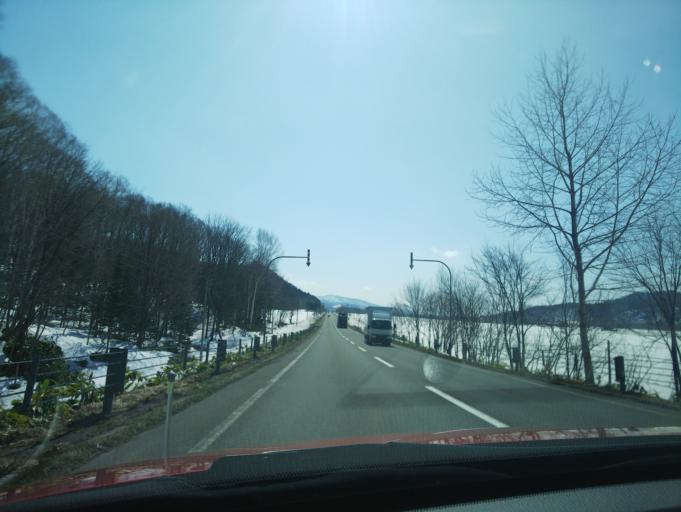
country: JP
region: Hokkaido
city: Nayoro
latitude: 44.6345
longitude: 142.2782
